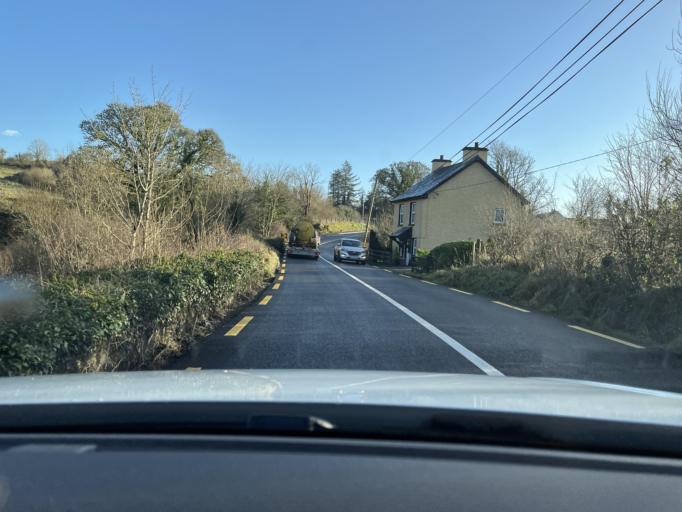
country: IE
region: Connaught
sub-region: County Leitrim
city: Manorhamilton
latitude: 54.1751
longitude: -8.1528
